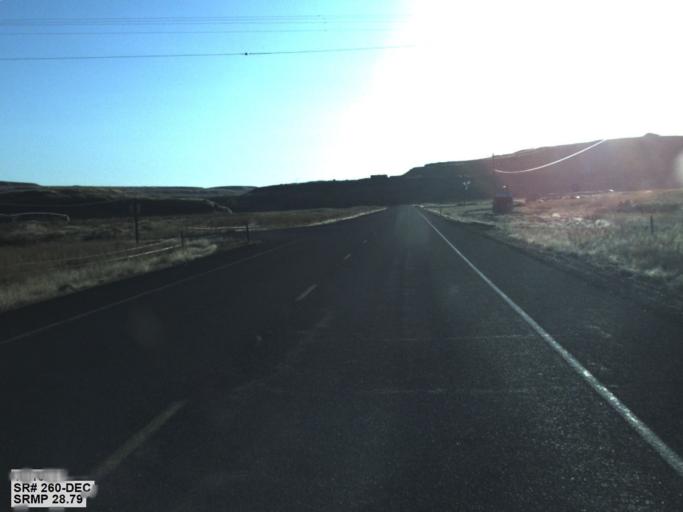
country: US
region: Washington
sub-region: Franklin County
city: Connell
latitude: 46.6642
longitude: -118.4838
